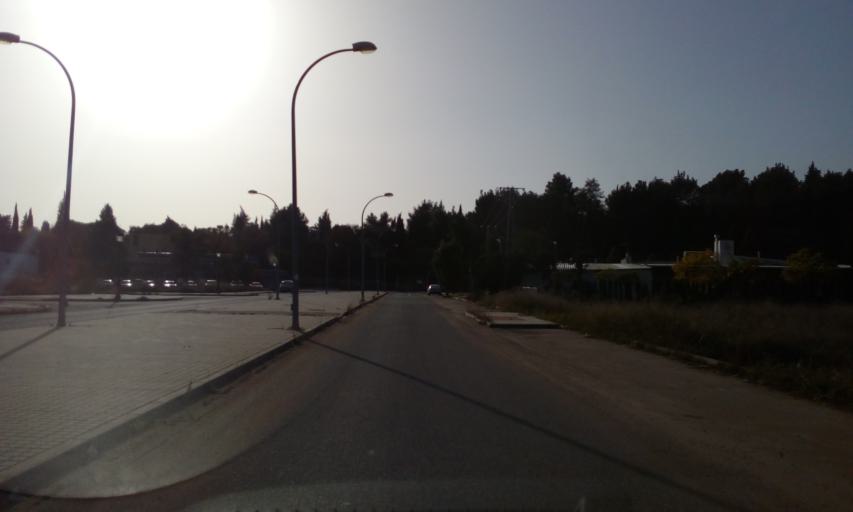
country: ES
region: Andalusia
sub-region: Provincia de Sevilla
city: Santiponce
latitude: 37.4455
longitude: -6.0438
